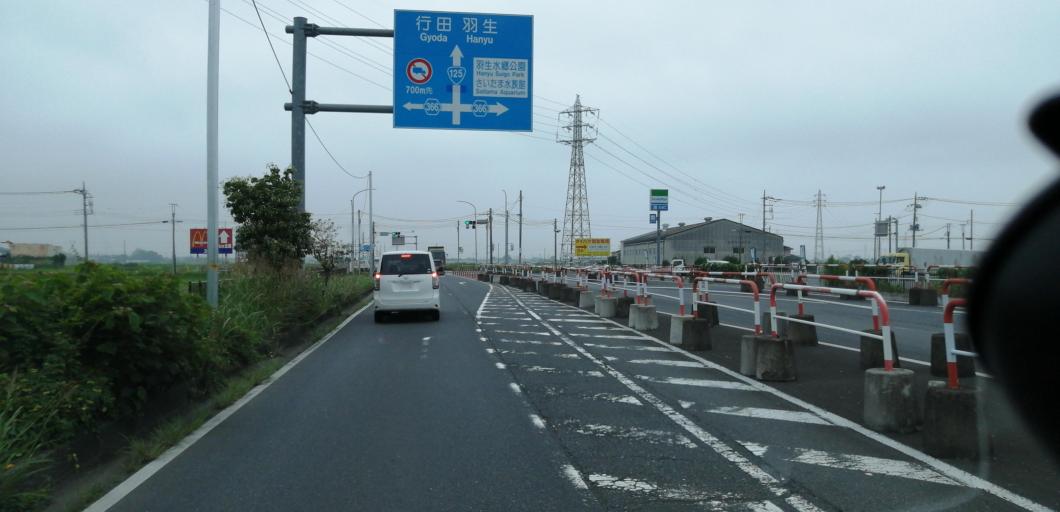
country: JP
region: Saitama
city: Kazo
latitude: 36.1404
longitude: 139.5910
